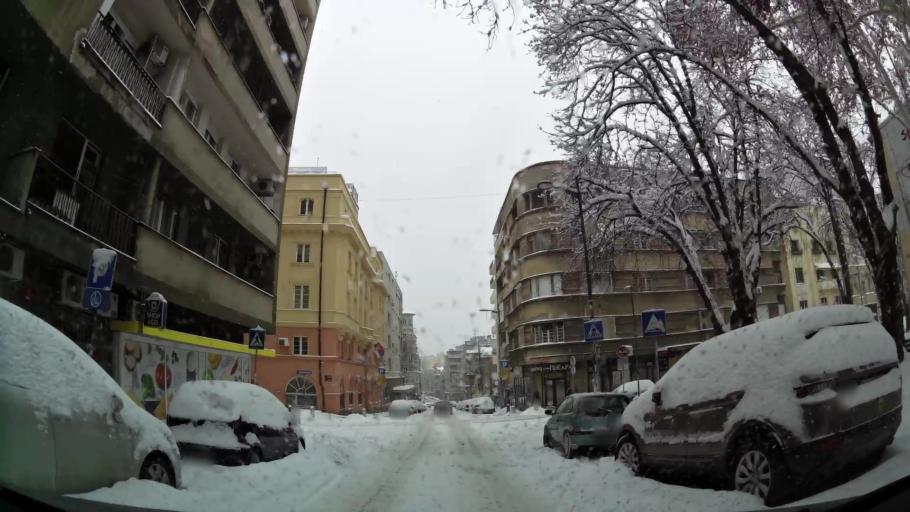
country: RS
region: Central Serbia
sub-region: Belgrade
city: Stari Grad
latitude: 44.8222
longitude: 20.4582
